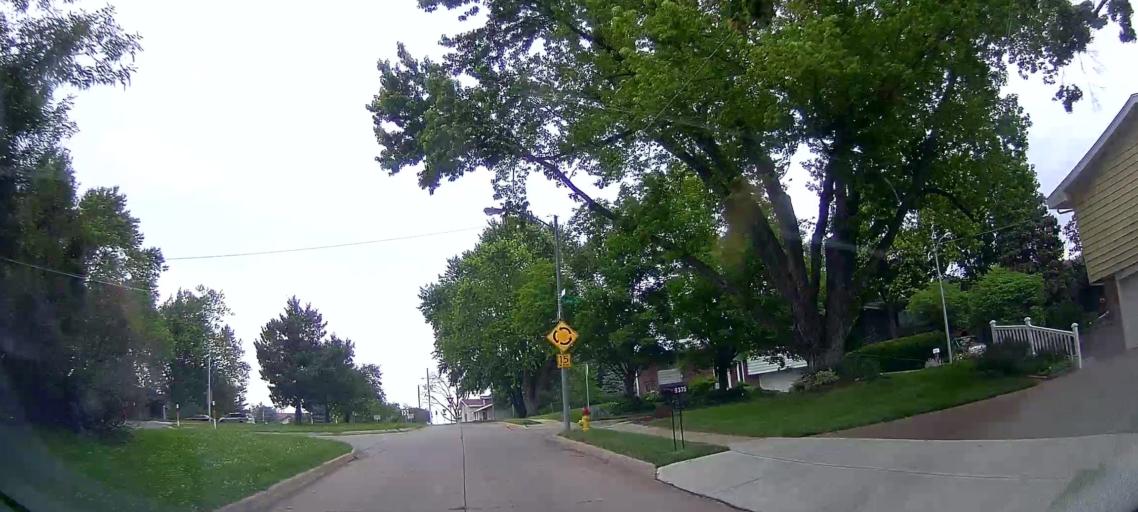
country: US
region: Nebraska
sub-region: Douglas County
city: Ralston
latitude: 41.3114
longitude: -96.0599
